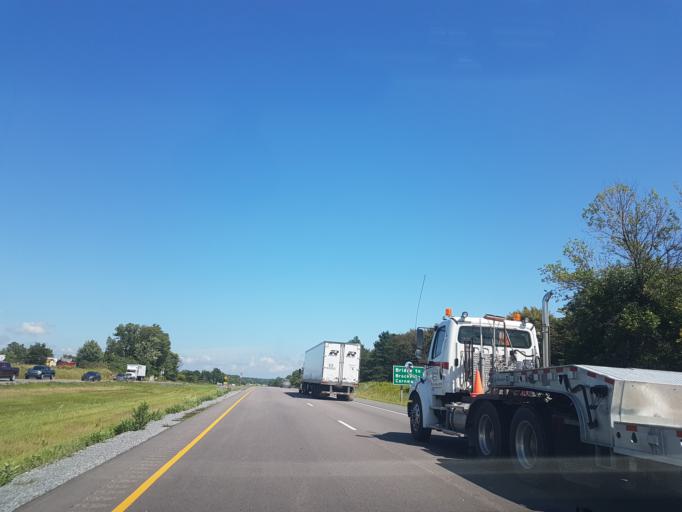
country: CA
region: Ontario
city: Gananoque
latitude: 44.3449
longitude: -76.1271
